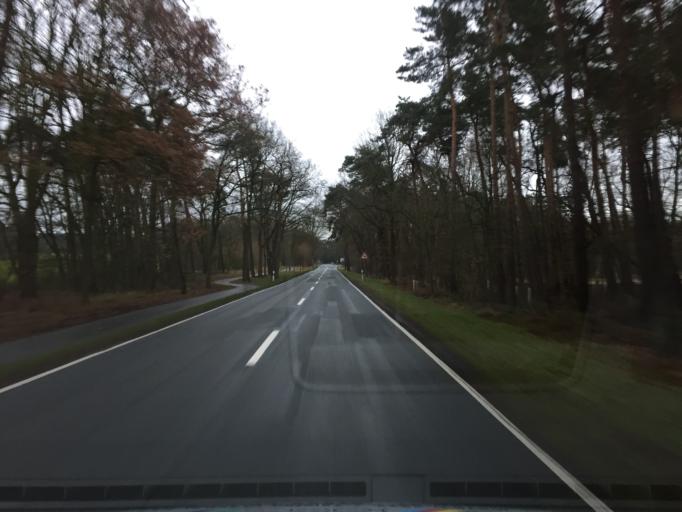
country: DE
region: Lower Saxony
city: Steyerberg
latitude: 52.5794
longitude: 8.9991
